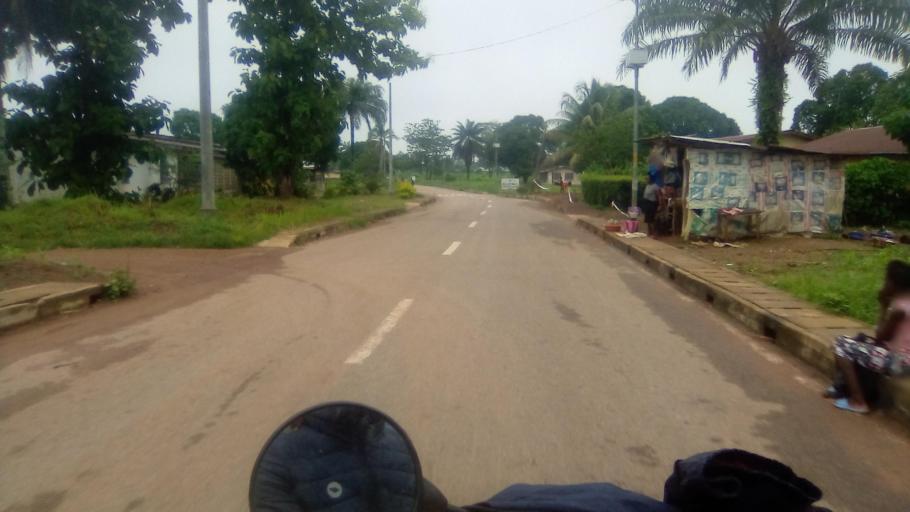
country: SL
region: Southern Province
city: Moyamba
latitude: 8.1497
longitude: -12.4349
